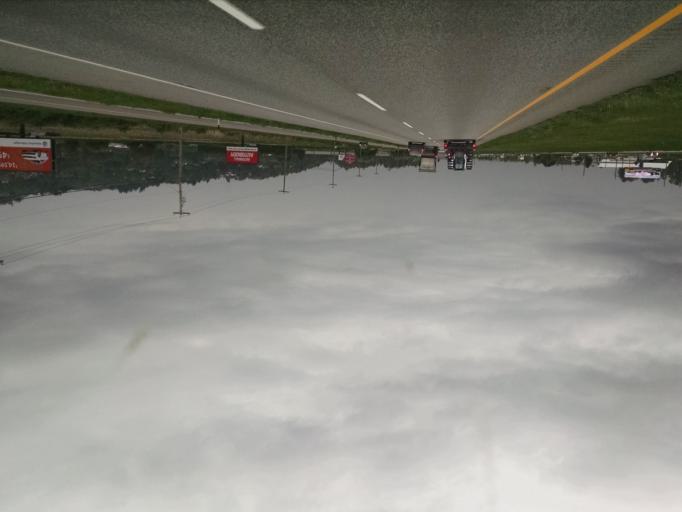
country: CA
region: British Columbia
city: Abbotsford
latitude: 49.0499
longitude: -122.1960
